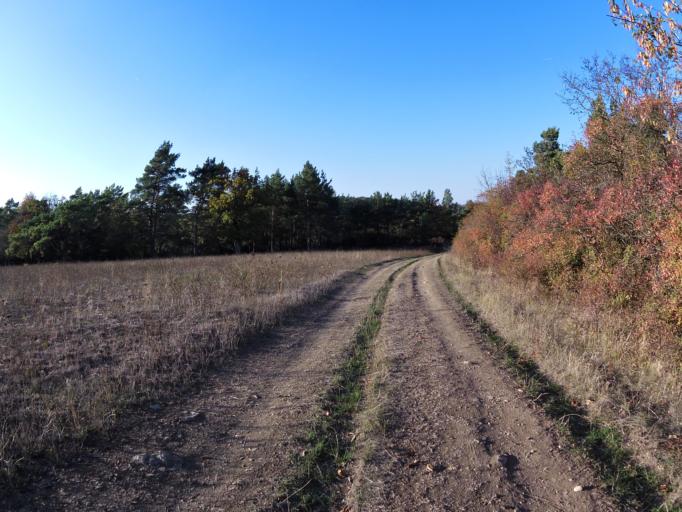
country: DE
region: Bavaria
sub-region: Regierungsbezirk Unterfranken
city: Eibelstadt
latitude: 49.7189
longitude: 9.9886
